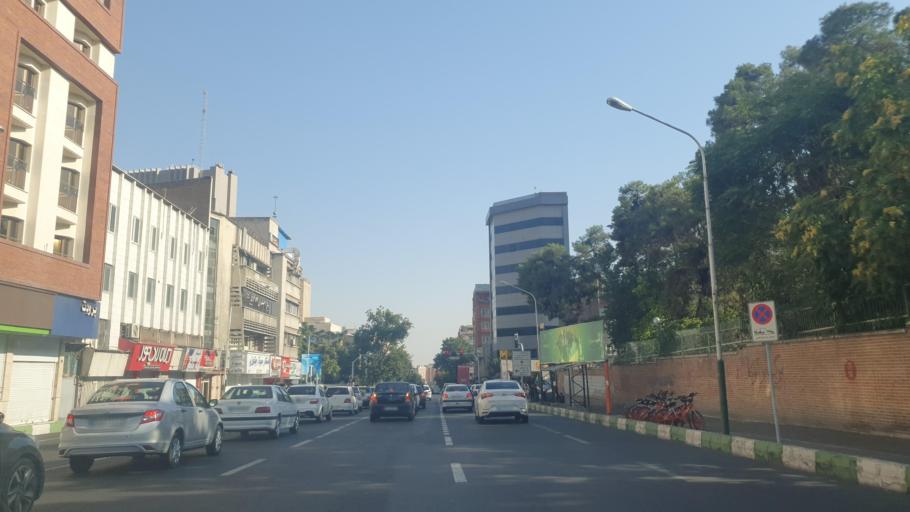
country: IR
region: Tehran
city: Tehran
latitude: 35.7079
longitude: 51.4257
